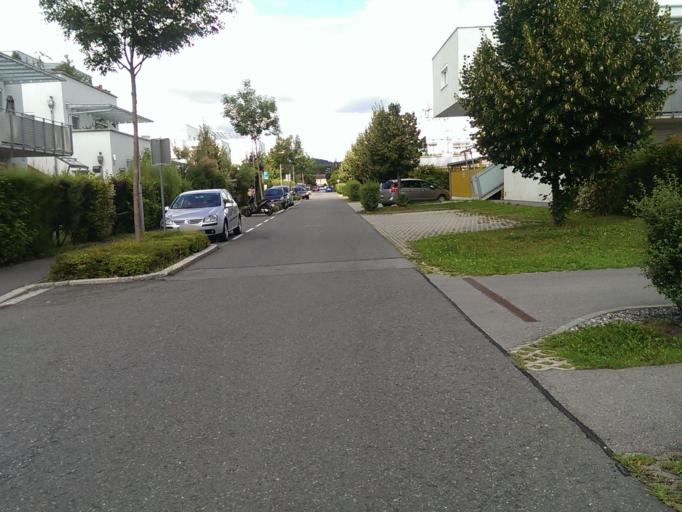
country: AT
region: Styria
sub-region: Graz Stadt
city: Graz
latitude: 47.0521
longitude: 15.4585
